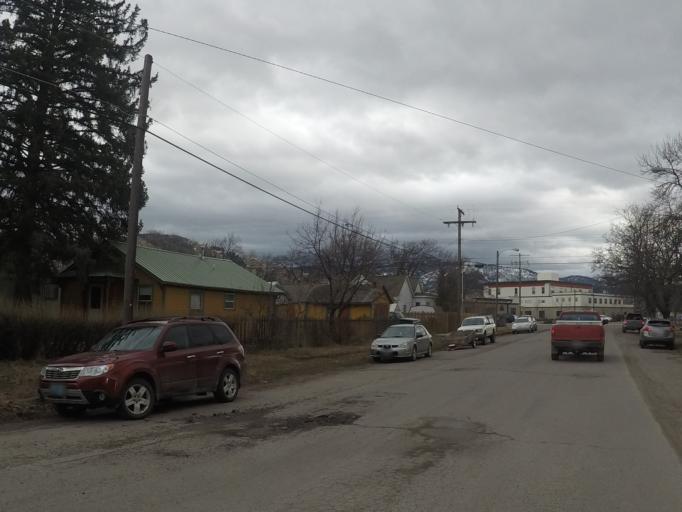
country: US
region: Montana
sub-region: Missoula County
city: Missoula
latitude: 46.8789
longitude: -114.0048
